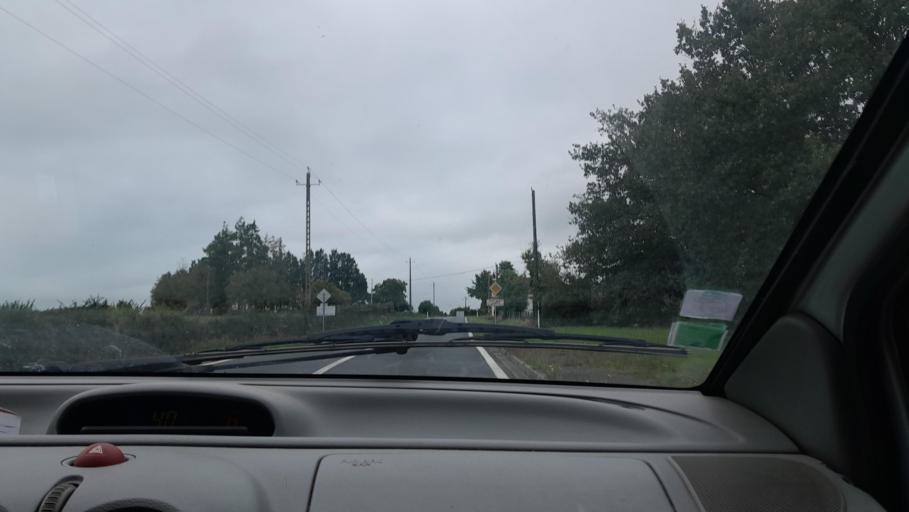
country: FR
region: Pays de la Loire
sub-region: Departement de la Loire-Atlantique
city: Saint-Mars-la-Jaille
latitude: 47.5340
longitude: -1.1865
